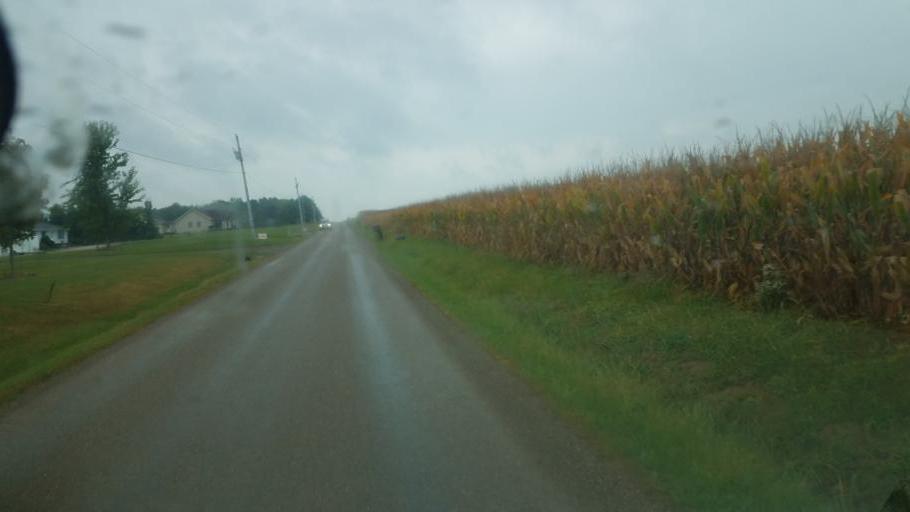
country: US
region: Ohio
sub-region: Ashland County
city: Ashland
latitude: 40.7925
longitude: -82.3689
